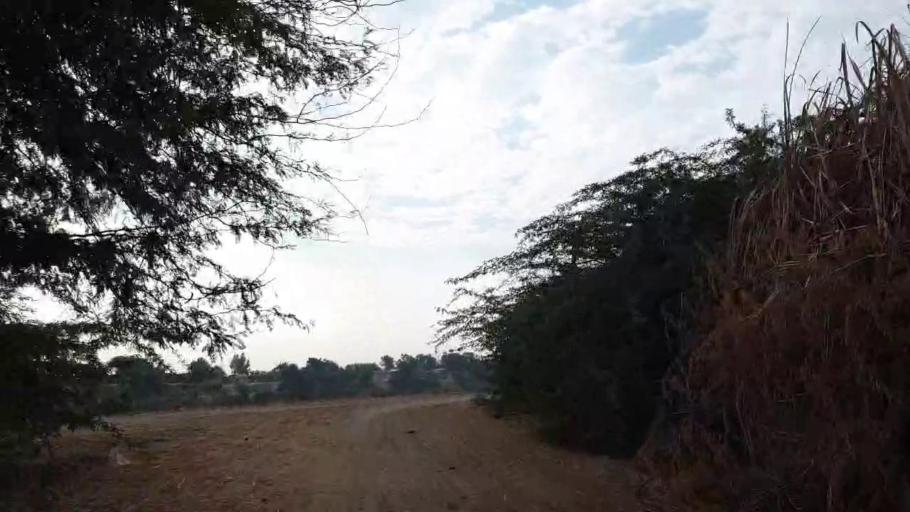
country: PK
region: Sindh
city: Tando Muhammad Khan
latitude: 25.0957
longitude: 68.4151
